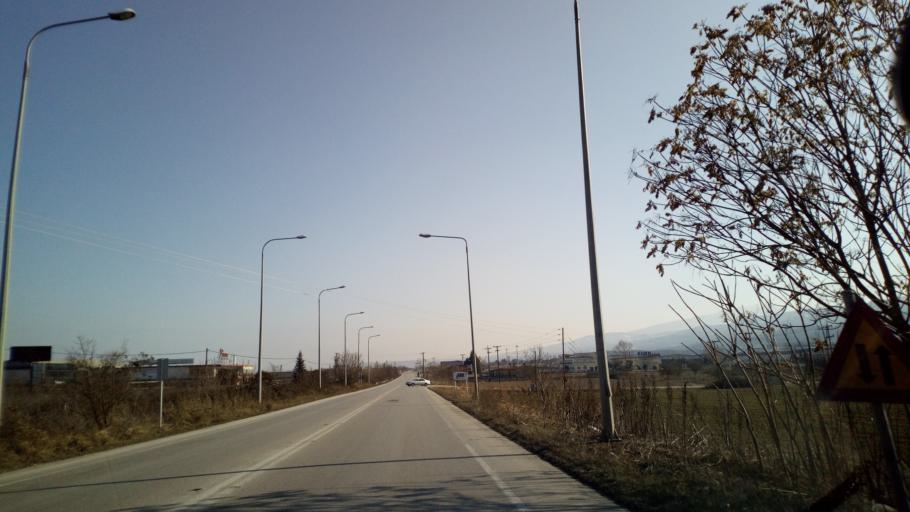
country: GR
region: Central Macedonia
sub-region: Nomos Thessalonikis
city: Kavallari
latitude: 40.7009
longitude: 23.0484
